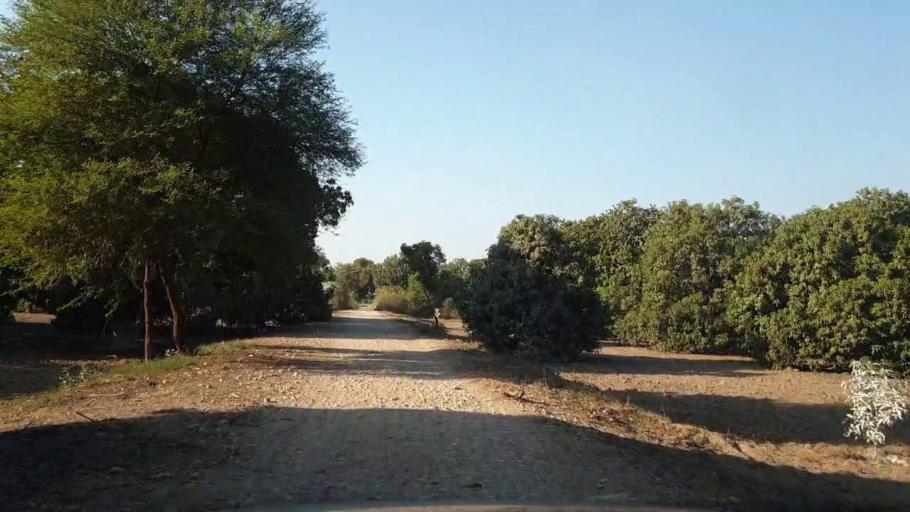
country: PK
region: Sindh
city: Tando Allahyar
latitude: 25.4932
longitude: 68.6426
